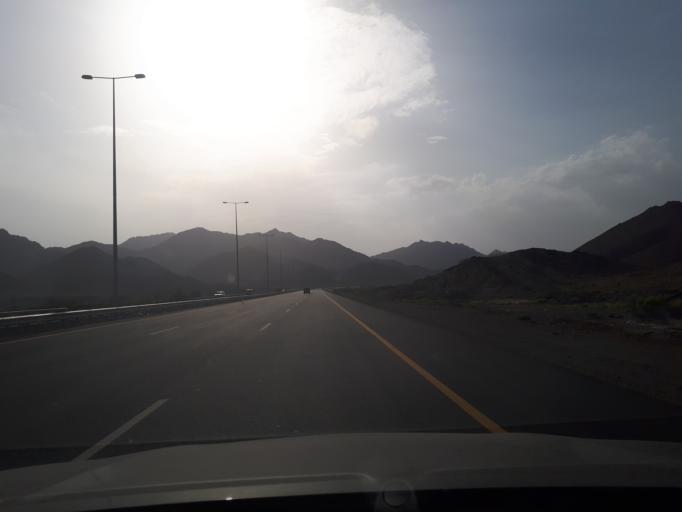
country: OM
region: Ash Sharqiyah
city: Ibra'
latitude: 22.8486
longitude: 58.3252
